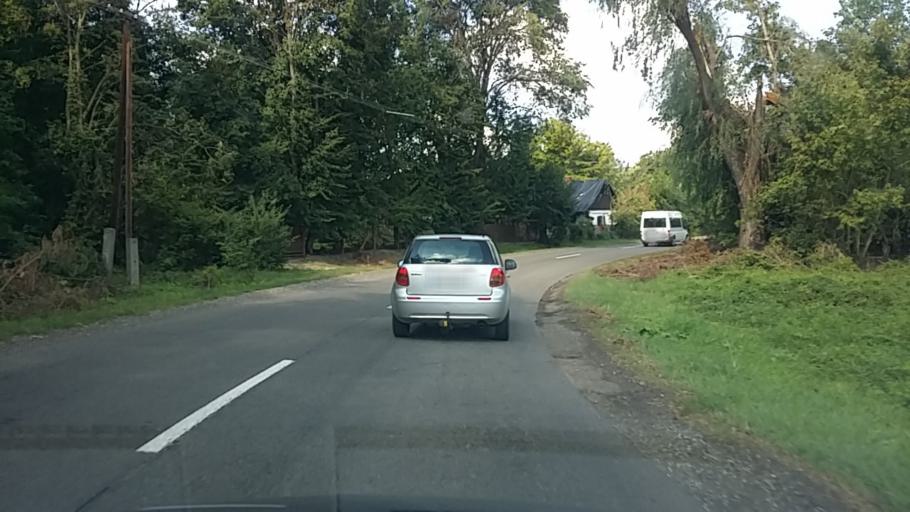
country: HU
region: Bacs-Kiskun
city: Tiszaalpar
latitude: 46.8426
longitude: 19.9778
